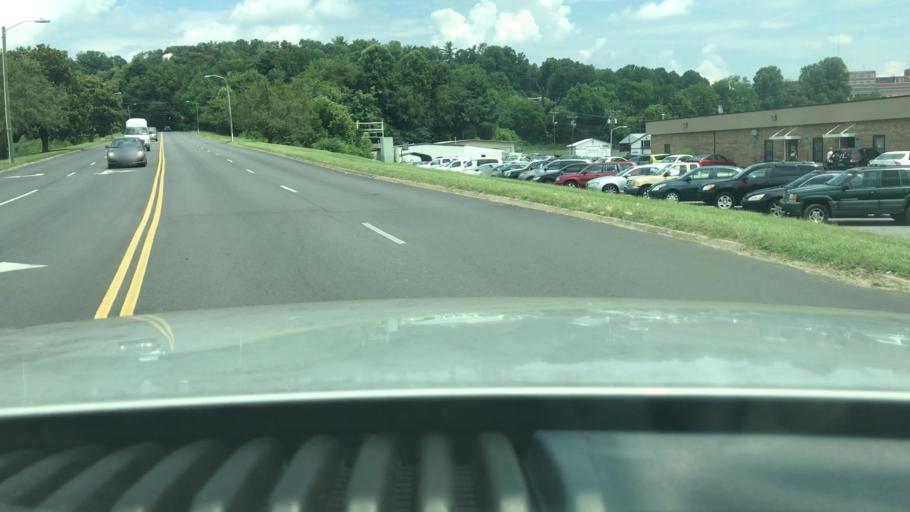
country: US
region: North Carolina
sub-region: Wilkes County
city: Wilkesboro
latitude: 36.1543
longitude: -81.1600
